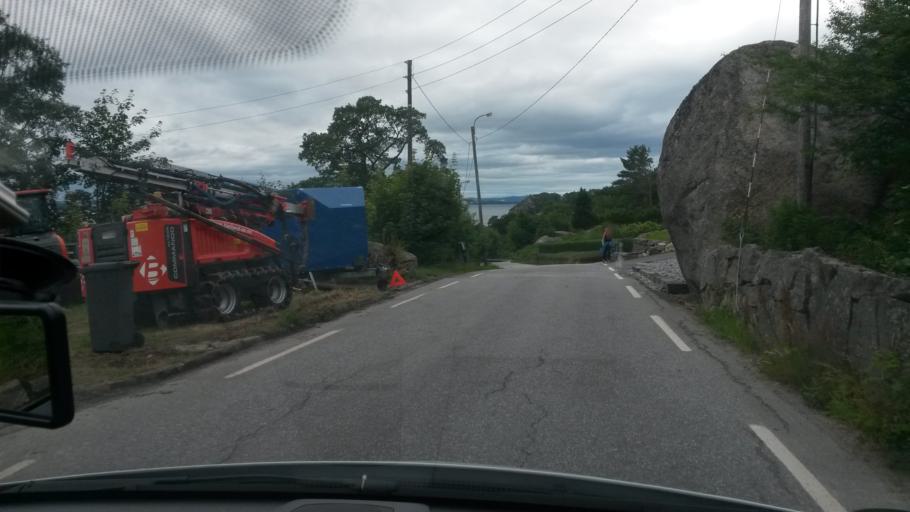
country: NO
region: Rogaland
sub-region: Sandnes
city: Sandnes
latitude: 58.8807
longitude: 5.7756
